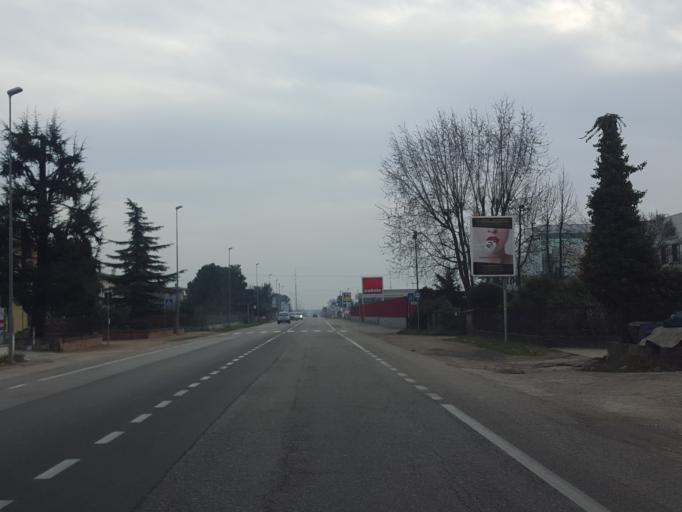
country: IT
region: Veneto
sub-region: Provincia di Verona
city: San Bonifacio
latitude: 45.3849
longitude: 11.2820
